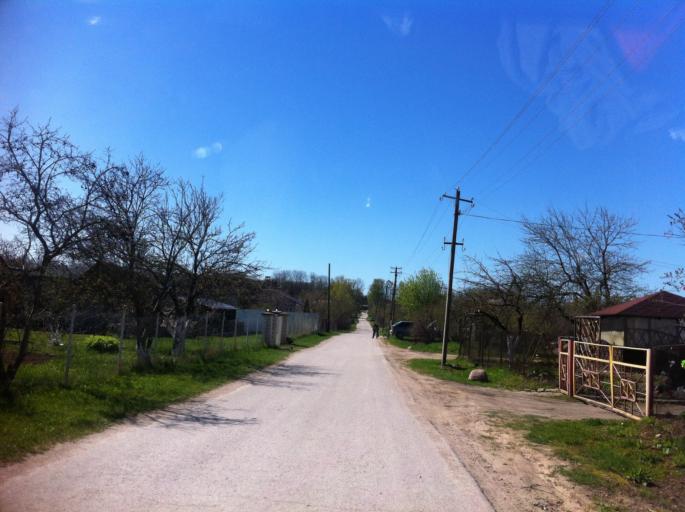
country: RU
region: Pskov
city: Izborsk
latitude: 57.7790
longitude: 27.9797
